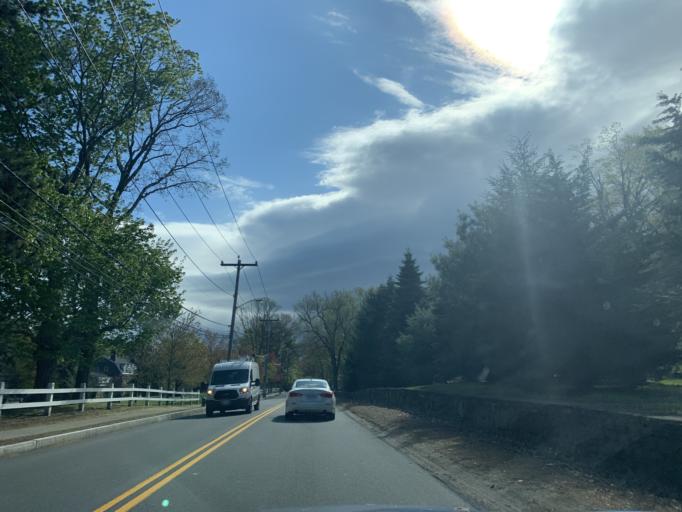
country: US
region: Massachusetts
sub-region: Norfolk County
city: Milton
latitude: 42.2575
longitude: -71.0656
